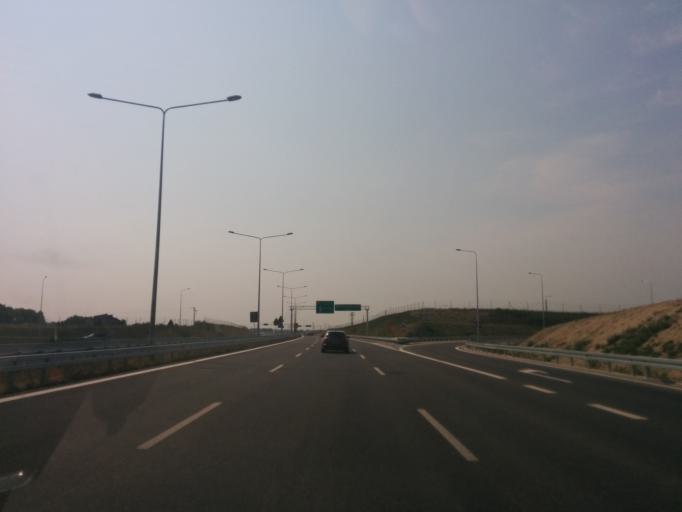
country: PL
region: Masovian Voivodeship
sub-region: Powiat pruszkowski
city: Nowe Grocholice
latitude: 52.1433
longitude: 20.8852
